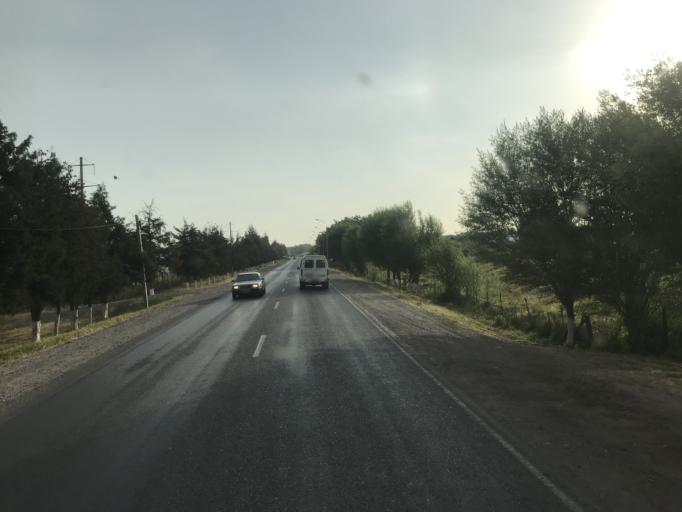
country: KZ
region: Ongtustik Qazaqstan
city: Saryaghash
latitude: 41.4855
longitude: 69.2554
